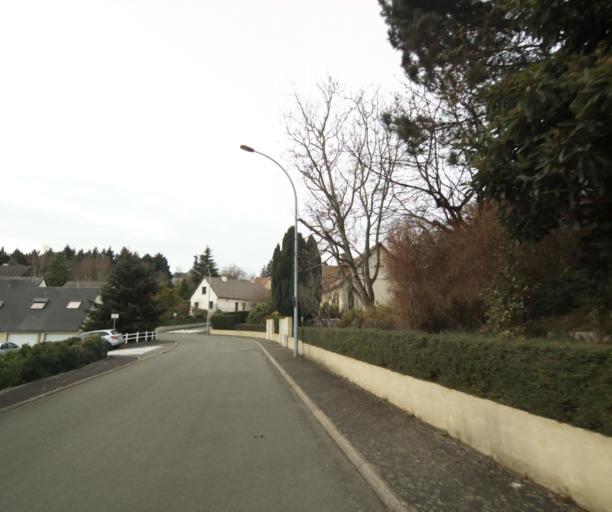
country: FR
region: Pays de la Loire
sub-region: Departement de la Sarthe
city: Le Mans
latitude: 48.0019
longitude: 0.2236
